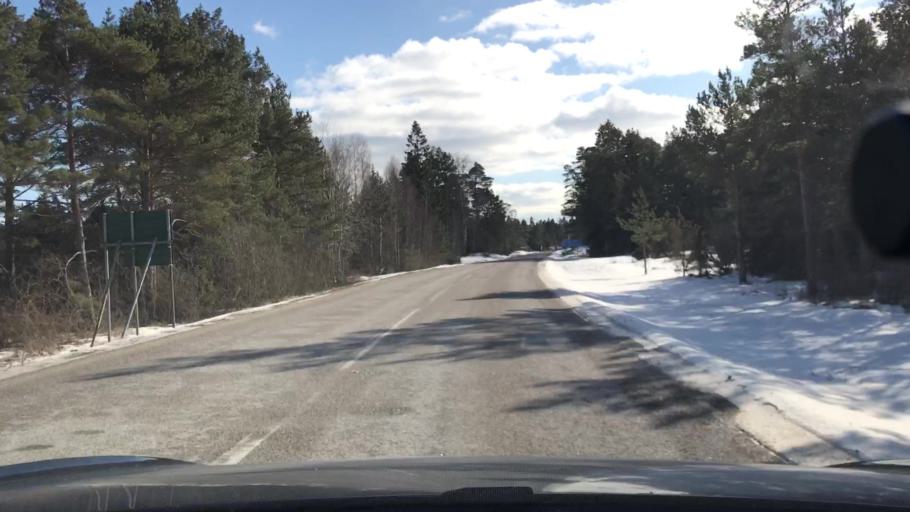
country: SE
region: Gotland
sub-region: Gotland
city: Hemse
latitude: 57.3438
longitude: 18.6932
